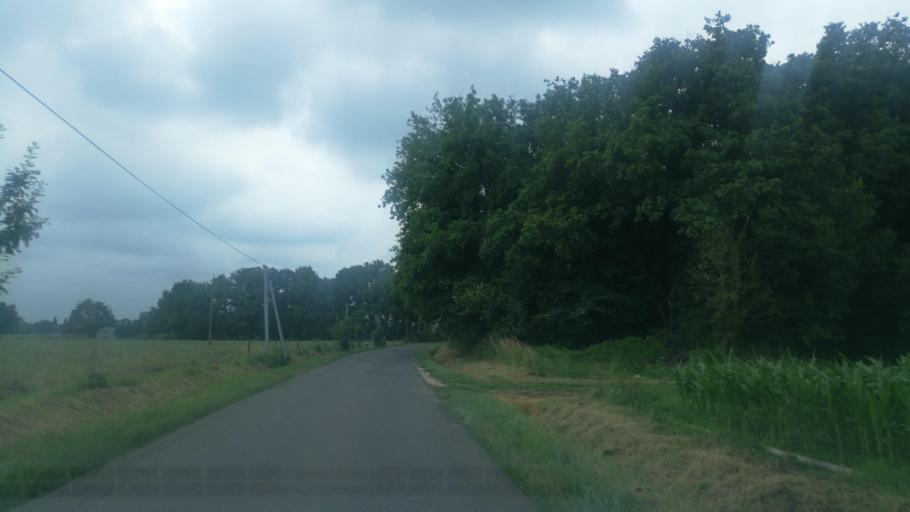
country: FR
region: Centre
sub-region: Departement du Loir-et-Cher
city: Saint-Romain-sur-Cher
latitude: 47.3408
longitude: 1.4508
